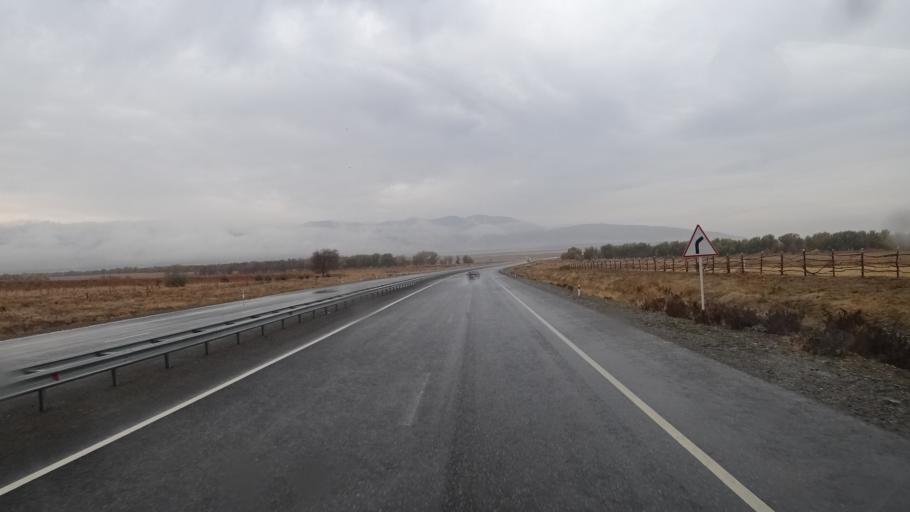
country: KZ
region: Ongtustik Qazaqstan
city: Kokterek
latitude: 42.5437
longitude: 70.2244
